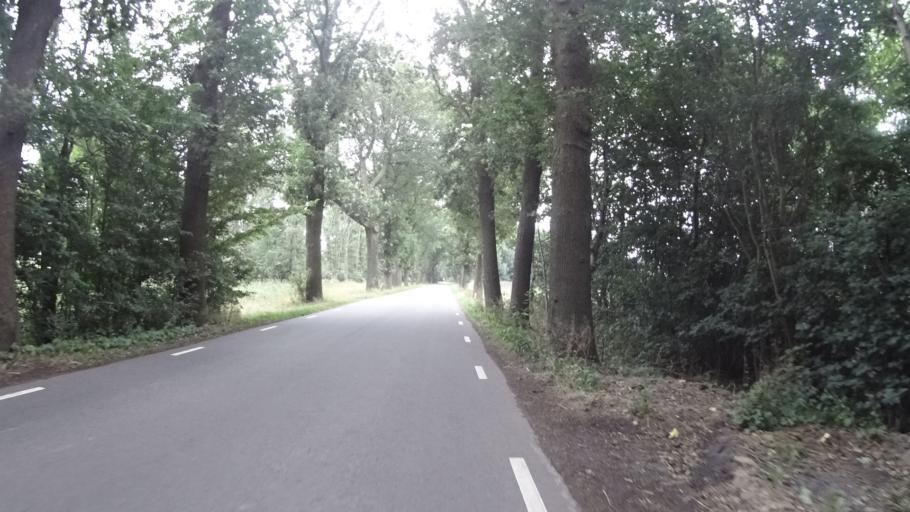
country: NL
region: Groningen
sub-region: Gemeente Slochteren
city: Slochteren
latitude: 53.2013
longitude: 6.8381
